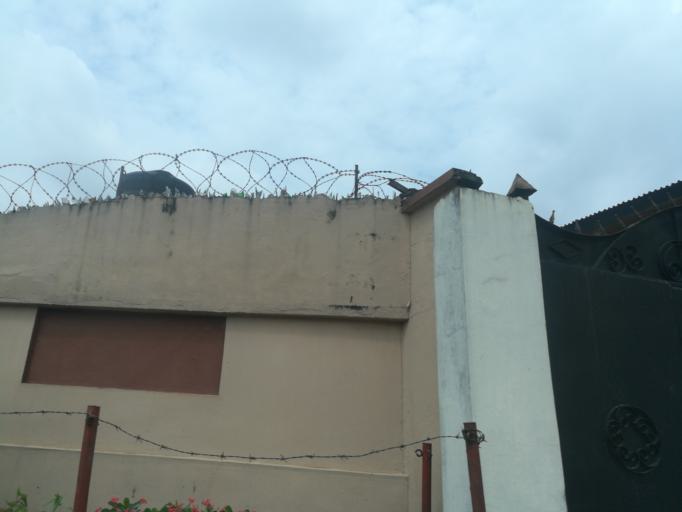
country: NG
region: Lagos
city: Ojota
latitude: 6.5759
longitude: 3.3680
